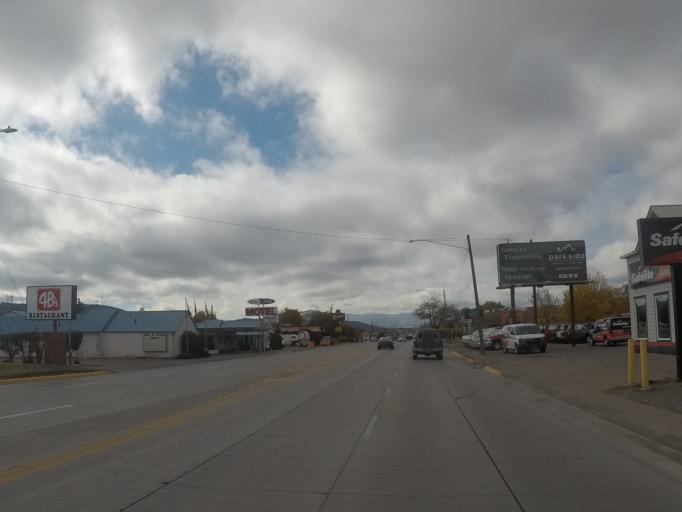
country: US
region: Montana
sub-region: Flathead County
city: Kalispell
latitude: 48.2041
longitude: -114.3034
